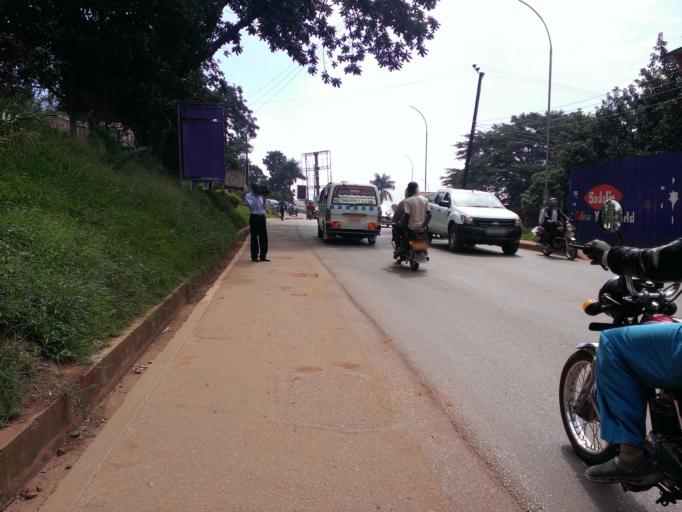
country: UG
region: Central Region
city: Kampala Central Division
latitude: 0.3133
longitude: 32.5606
